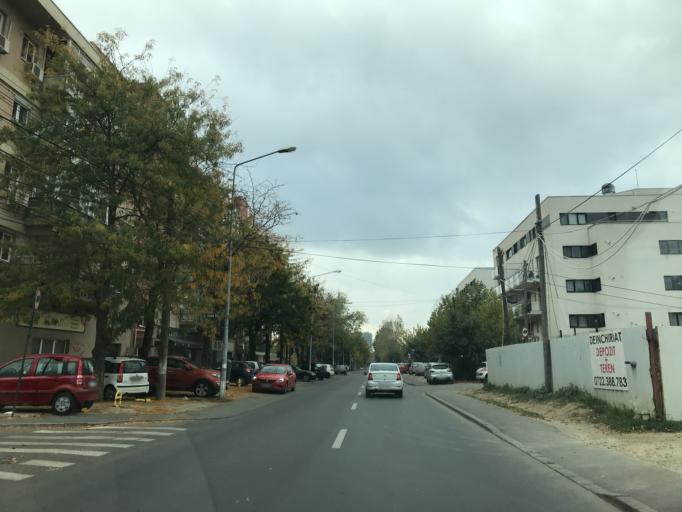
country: RO
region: Ilfov
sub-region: Comuna Otopeni
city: Otopeni
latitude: 44.4900
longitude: 26.0647
